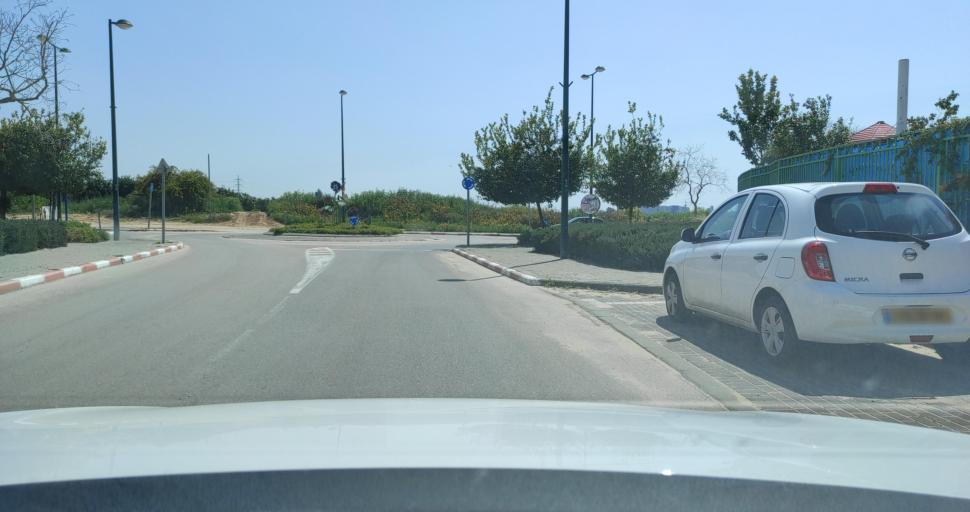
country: IL
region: Central District
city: Nordiyya
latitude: 32.2960
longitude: 34.8754
